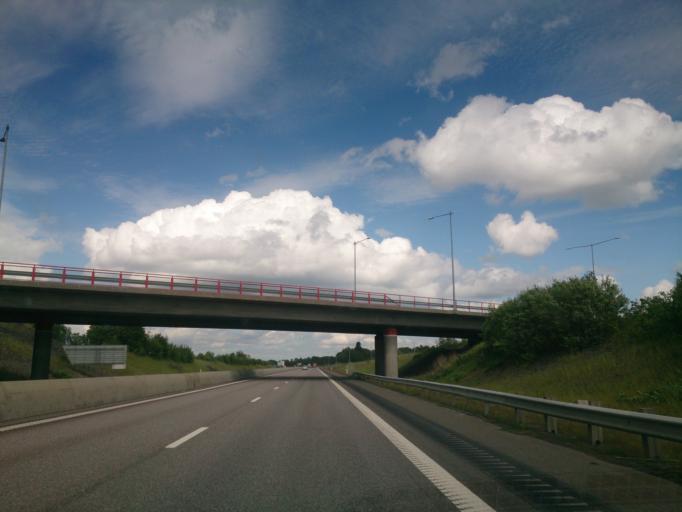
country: SE
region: OEstergoetland
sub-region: Norrkopings Kommun
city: Norrkoping
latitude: 58.5800
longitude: 16.1116
